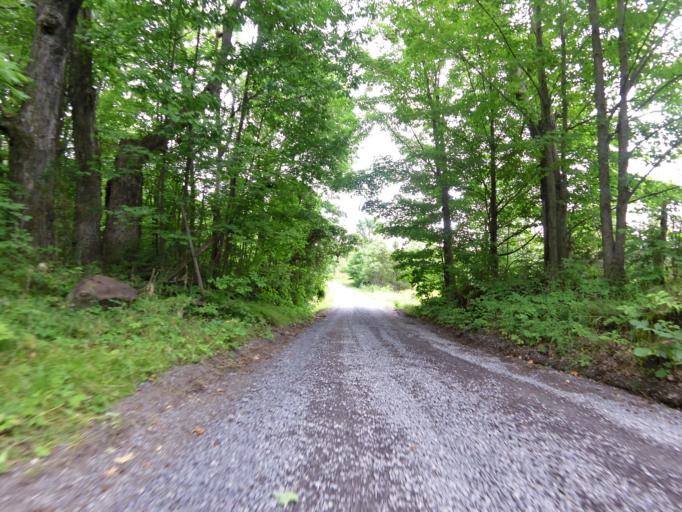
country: CA
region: Ontario
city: Kingston
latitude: 44.5638
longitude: -76.5892
